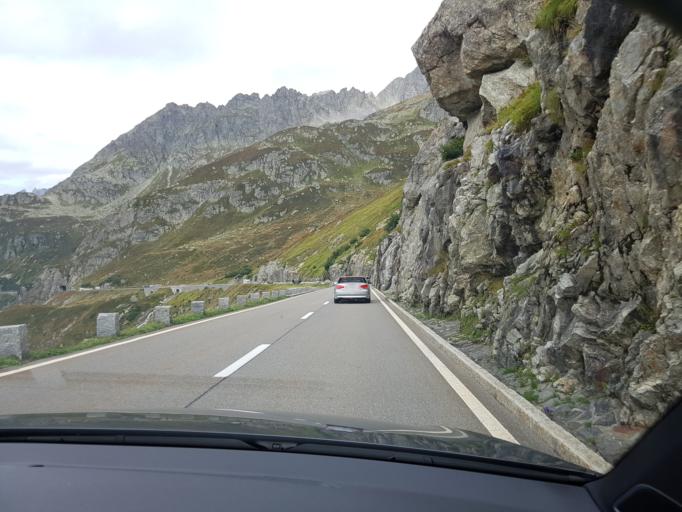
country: CH
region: Obwalden
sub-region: Obwalden
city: Engelberg
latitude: 46.7308
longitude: 8.4378
